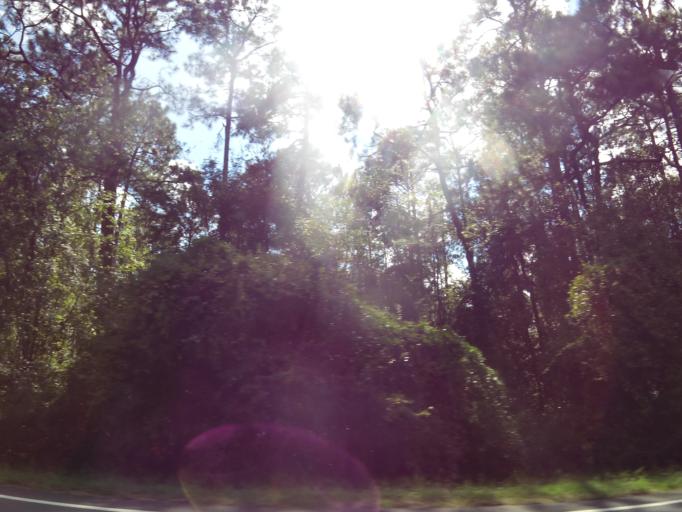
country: US
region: Georgia
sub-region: Echols County
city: Statenville
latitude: 30.7224
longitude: -83.0741
